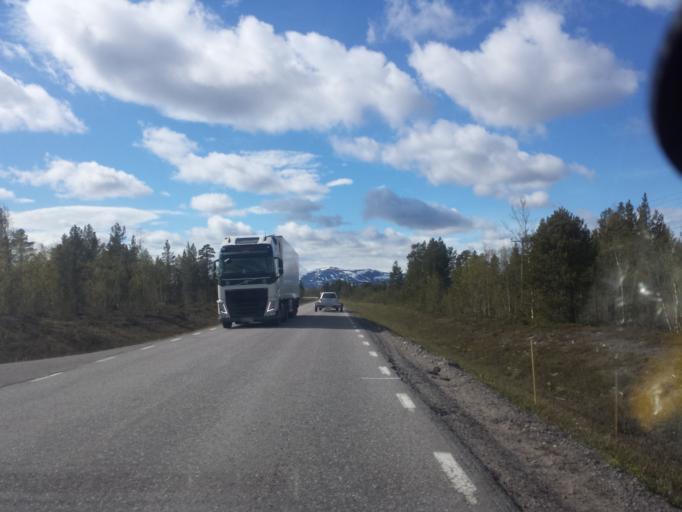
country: SE
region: Norrbotten
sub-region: Kiruna Kommun
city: Kiruna
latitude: 67.9928
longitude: 19.9126
